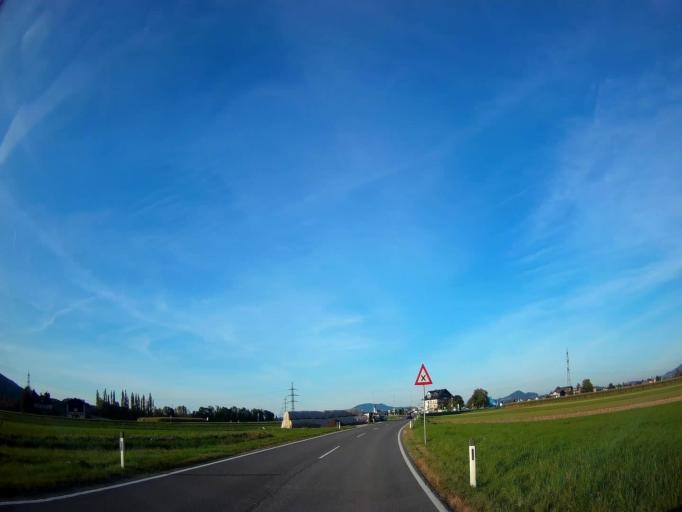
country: DE
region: Bavaria
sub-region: Upper Bavaria
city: Ainring
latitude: 47.7775
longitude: 12.9600
